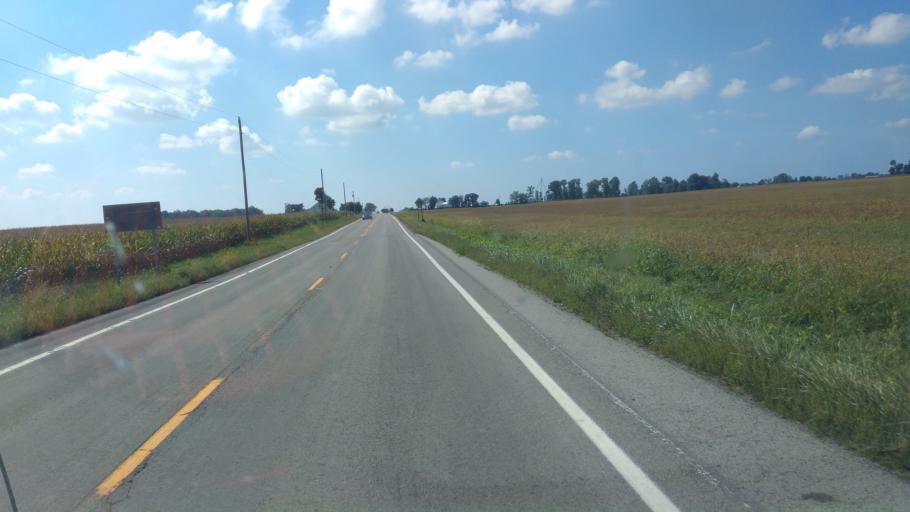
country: US
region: Ohio
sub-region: Logan County
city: Russells Point
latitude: 40.5869
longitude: -83.8443
